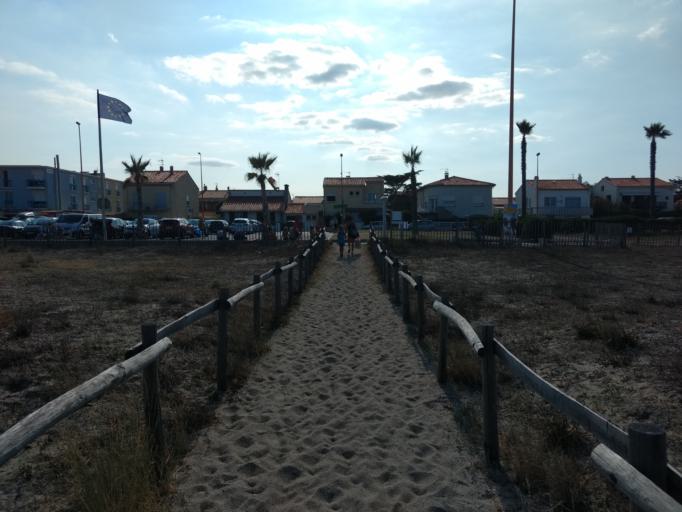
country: FR
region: Languedoc-Roussillon
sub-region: Departement des Pyrenees-Orientales
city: Le Barcares
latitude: 42.7882
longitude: 3.0386
